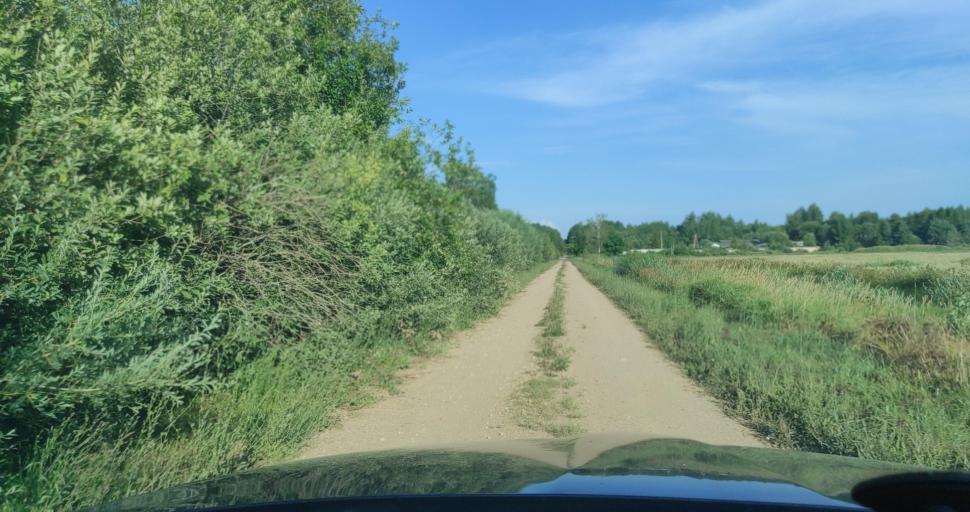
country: LV
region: Skrunda
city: Skrunda
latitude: 56.6765
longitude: 21.9879
